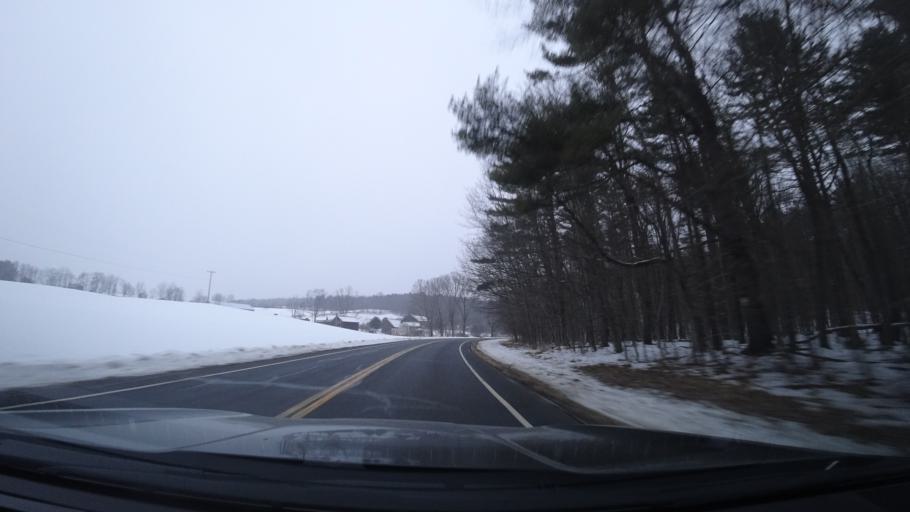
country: US
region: New York
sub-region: Washington County
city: Greenwich
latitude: 43.1575
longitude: -73.4213
